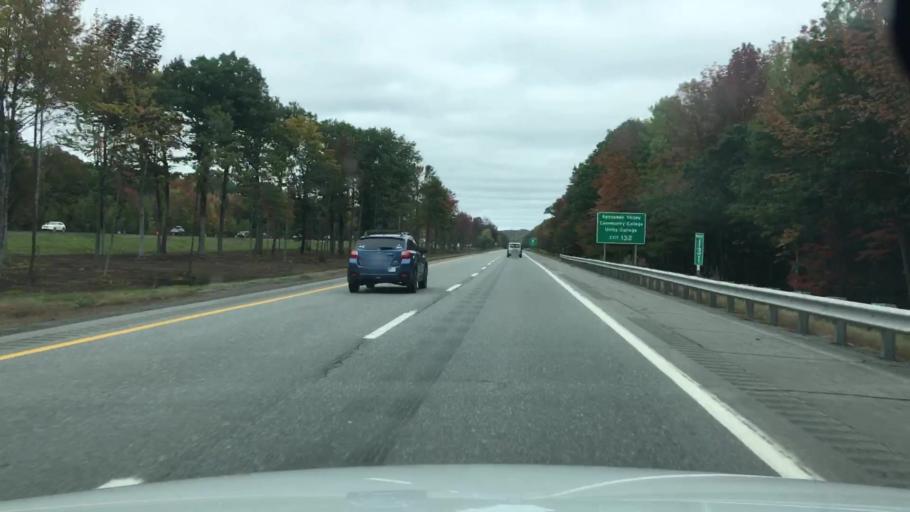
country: US
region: Maine
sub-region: Kennebec County
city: Waterville
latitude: 44.5768
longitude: -69.6298
